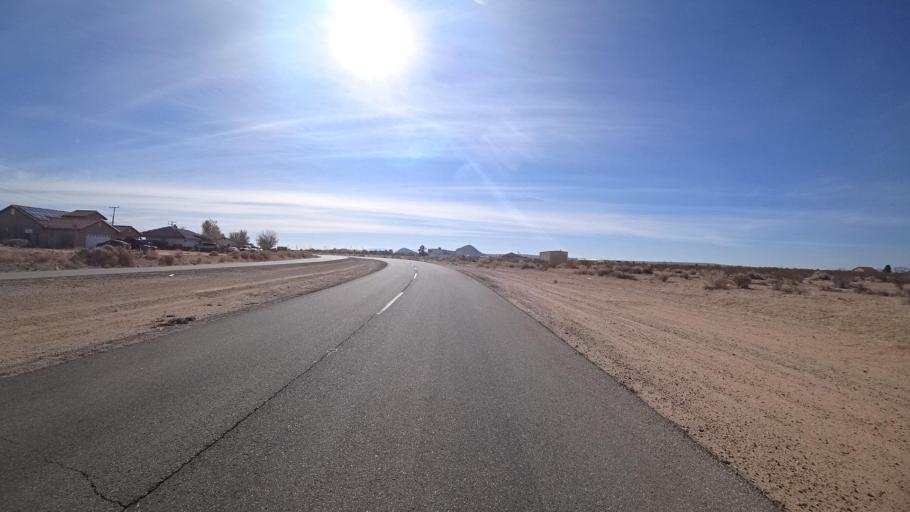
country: US
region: California
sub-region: Kern County
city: California City
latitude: 35.1219
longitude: -117.9410
